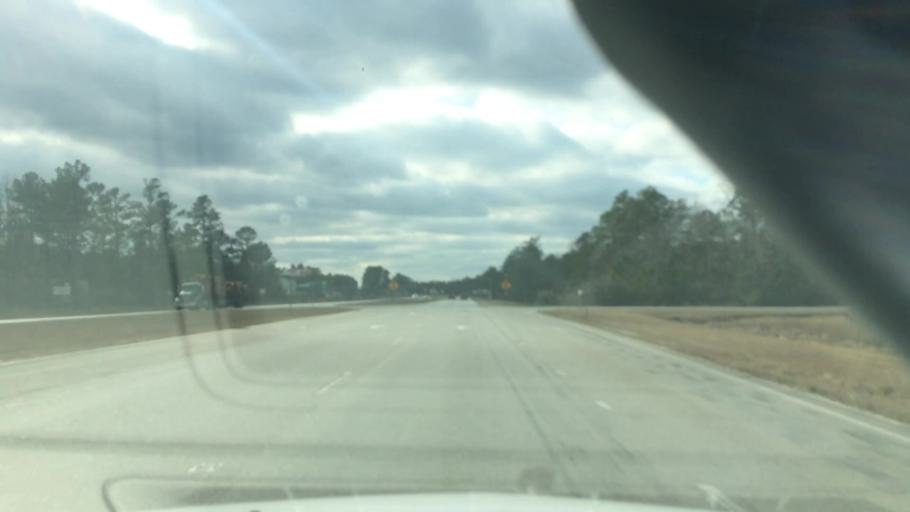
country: US
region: North Carolina
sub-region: Brunswick County
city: Bolivia
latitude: 34.0405
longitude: -78.2440
